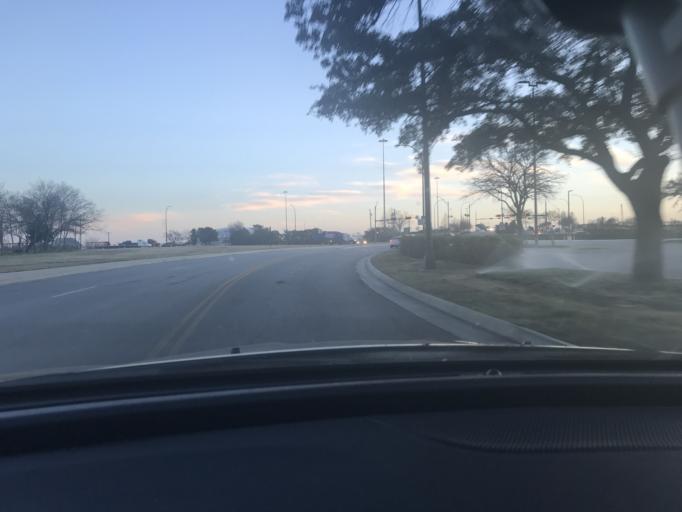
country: US
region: Texas
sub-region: Tarrant County
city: Arlington
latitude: 32.7631
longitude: -97.1019
